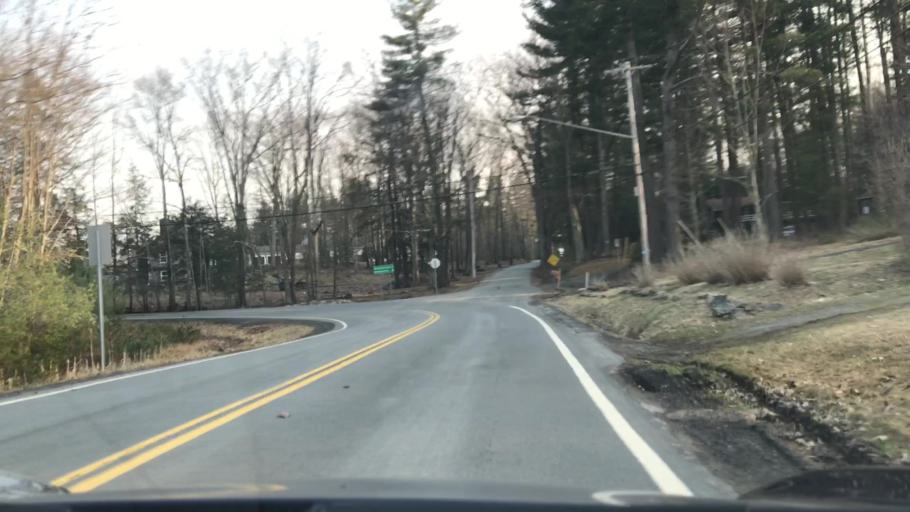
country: US
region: New York
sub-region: Sullivan County
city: Liberty
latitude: 41.6794
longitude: -74.9929
